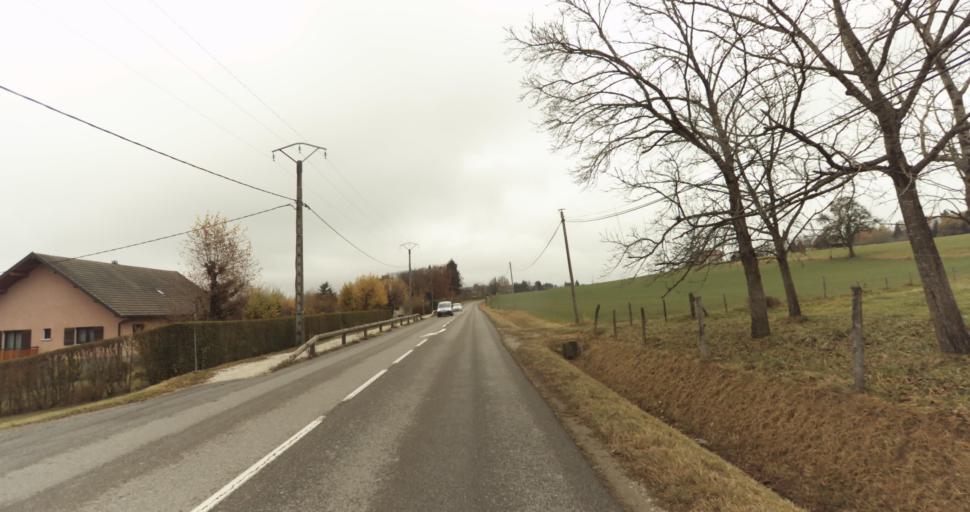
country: FR
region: Rhone-Alpes
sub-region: Departement de la Haute-Savoie
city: Groisy
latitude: 46.0071
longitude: 6.1617
